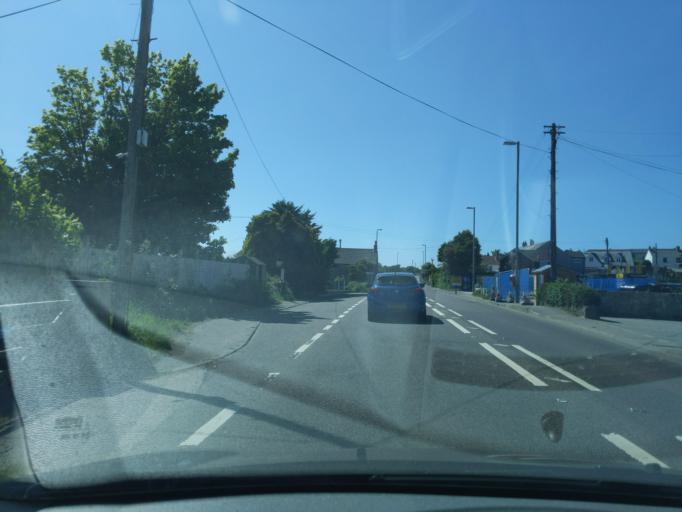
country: GB
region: England
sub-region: Cornwall
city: Penryn
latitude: 50.1640
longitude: -5.1586
